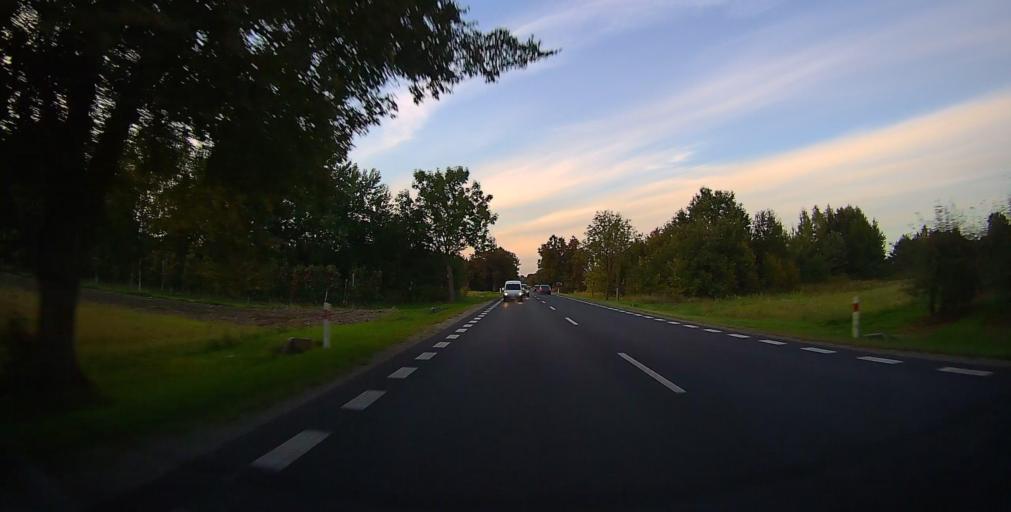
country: PL
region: Masovian Voivodeship
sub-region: Powiat kozienicki
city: Ryczywol
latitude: 51.7438
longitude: 21.3878
